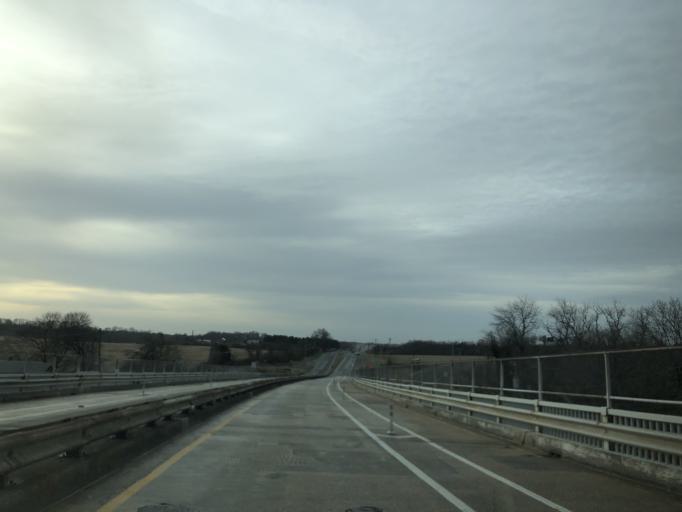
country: US
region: Delaware
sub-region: New Castle County
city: Delaware City
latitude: 39.5483
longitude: -75.6487
